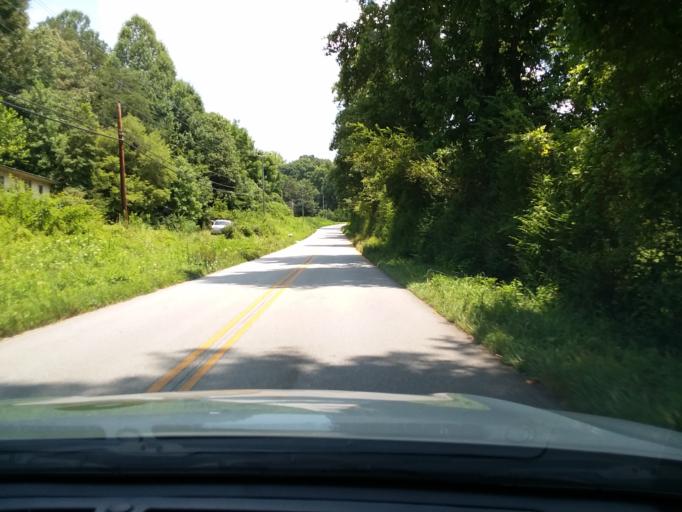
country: US
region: Georgia
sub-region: Rabun County
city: Clayton
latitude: 34.8013
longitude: -83.4268
